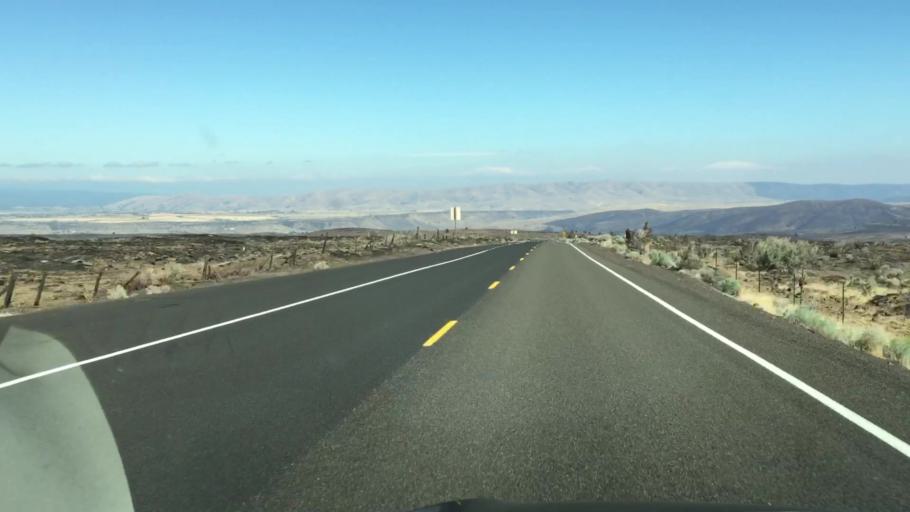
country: US
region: Oregon
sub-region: Jefferson County
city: Warm Springs
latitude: 45.1035
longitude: -121.0385
